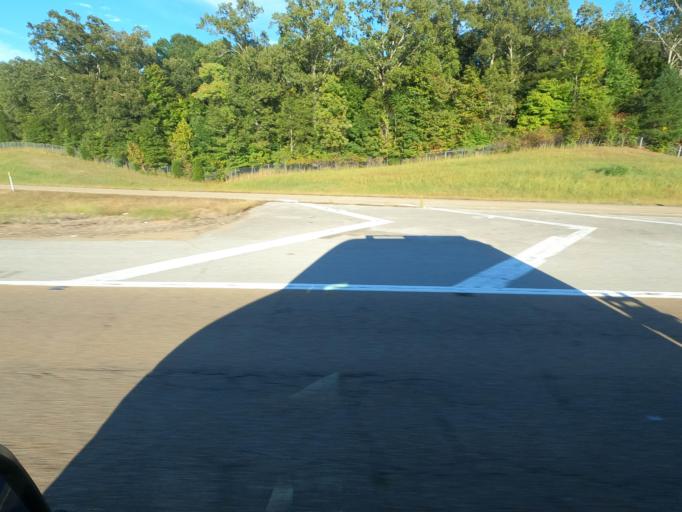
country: US
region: Tennessee
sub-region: Shelby County
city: Arlington
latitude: 35.2459
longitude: -89.6684
